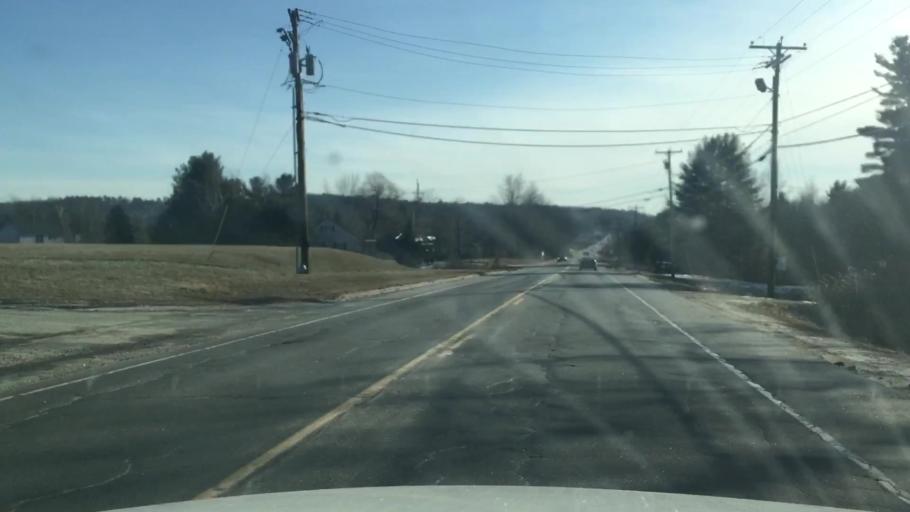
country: US
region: Maine
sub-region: Androscoggin County
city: Sabattus
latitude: 44.1090
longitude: -70.0896
